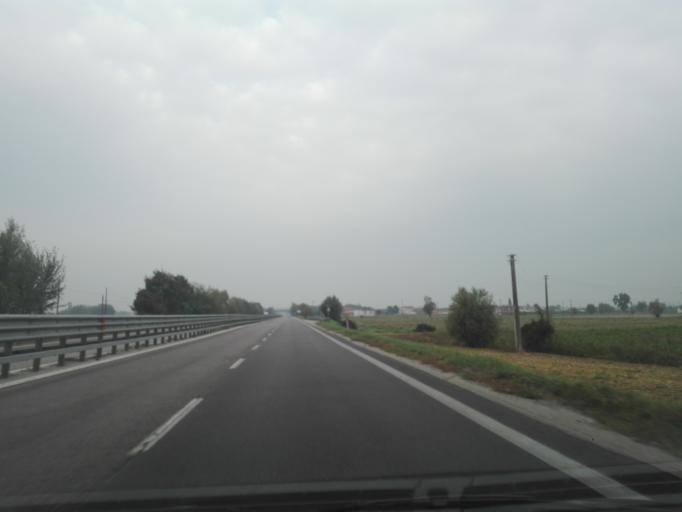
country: IT
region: Veneto
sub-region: Provincia di Verona
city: Spinimbecco
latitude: 45.1340
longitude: 11.3669
